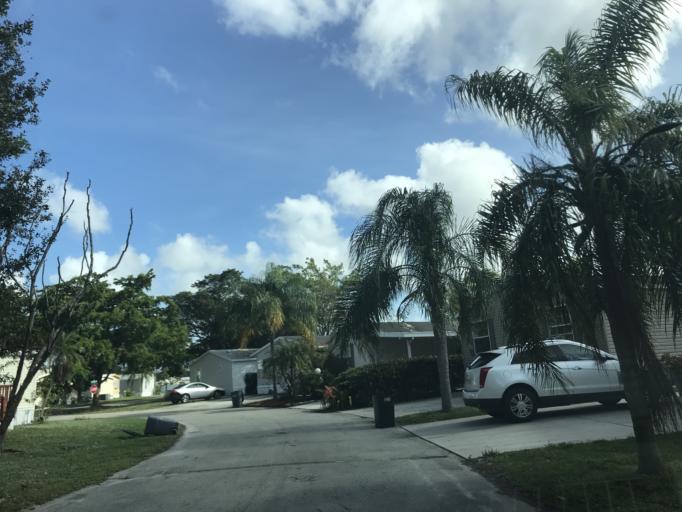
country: US
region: Florida
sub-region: Palm Beach County
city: Boca Pointe
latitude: 26.3095
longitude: -80.1760
